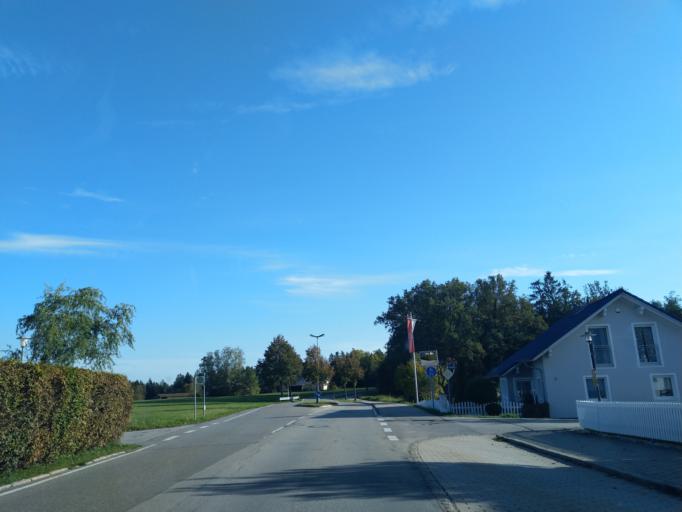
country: DE
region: Bavaria
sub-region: Lower Bavaria
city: Metten
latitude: 48.8807
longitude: 12.8977
